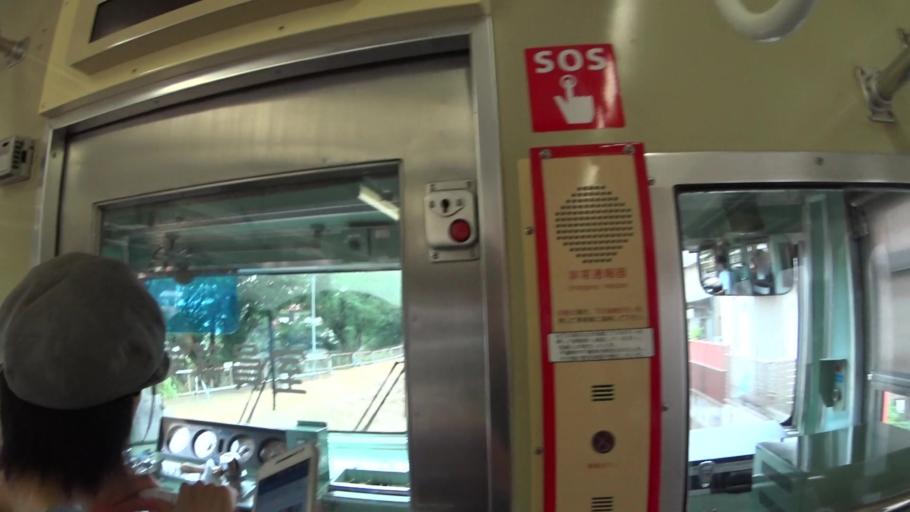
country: JP
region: Chiba
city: Nagareyama
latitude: 35.8236
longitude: 139.9179
